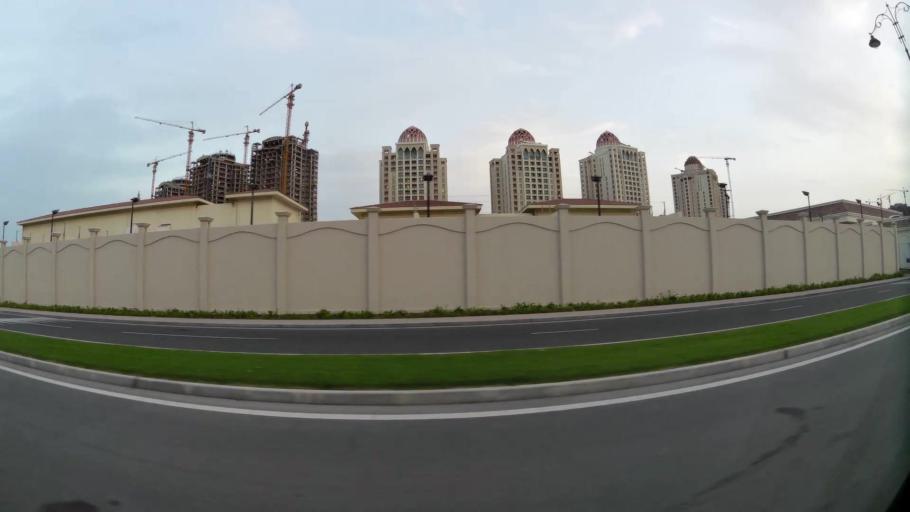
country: QA
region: Baladiyat ad Dawhah
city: Doha
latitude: 25.3728
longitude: 51.5562
